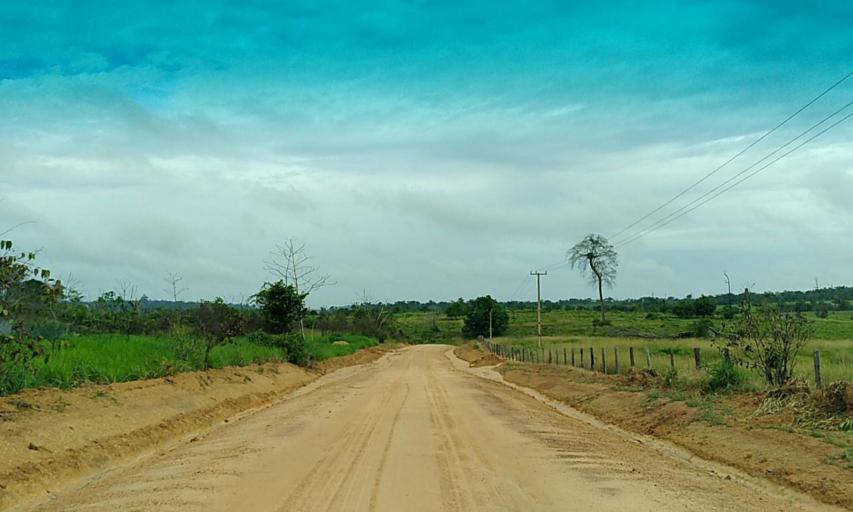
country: BR
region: Para
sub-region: Senador Jose Porfirio
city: Senador Jose Porfirio
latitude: -3.0426
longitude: -51.6782
